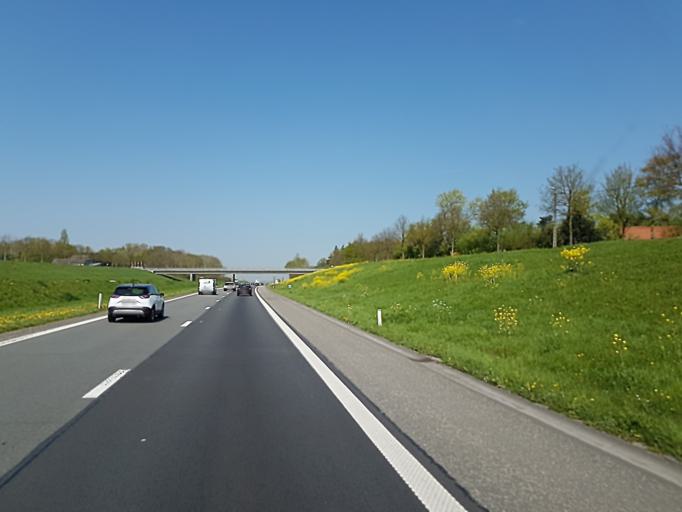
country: BE
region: Flanders
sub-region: Provincie West-Vlaanderen
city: Zonnebeke
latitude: 50.8465
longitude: 2.9835
